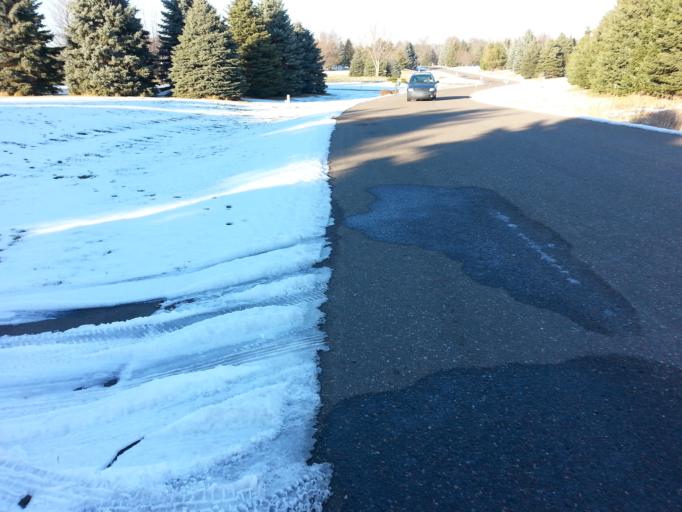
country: US
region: Minnesota
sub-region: Washington County
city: Lake Elmo
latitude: 44.9638
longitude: -92.8305
